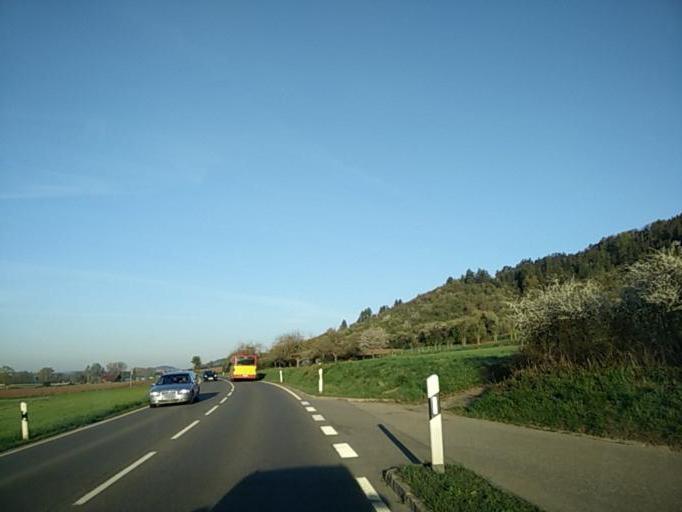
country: DE
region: Baden-Wuerttemberg
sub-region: Tuebingen Region
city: Tuebingen
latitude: 48.5251
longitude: 9.0065
